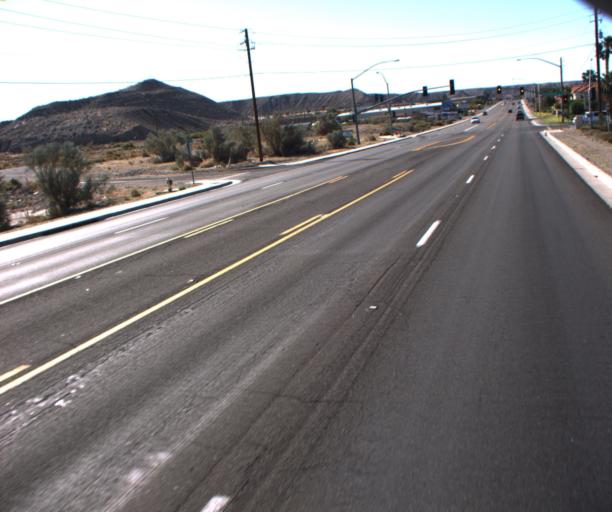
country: US
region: Arizona
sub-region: Mohave County
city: Bullhead City
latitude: 35.0771
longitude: -114.5938
